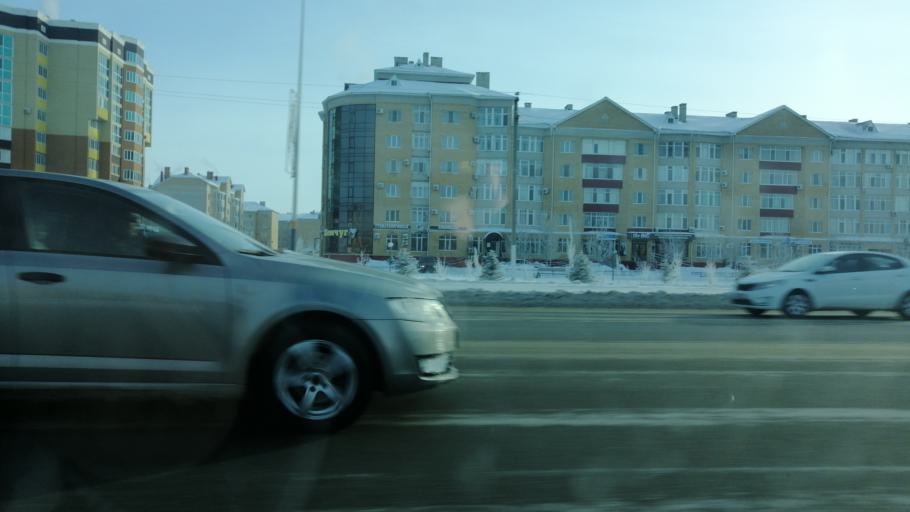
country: KZ
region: Aqtoebe
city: Aqtobe
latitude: 50.2839
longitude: 57.1415
